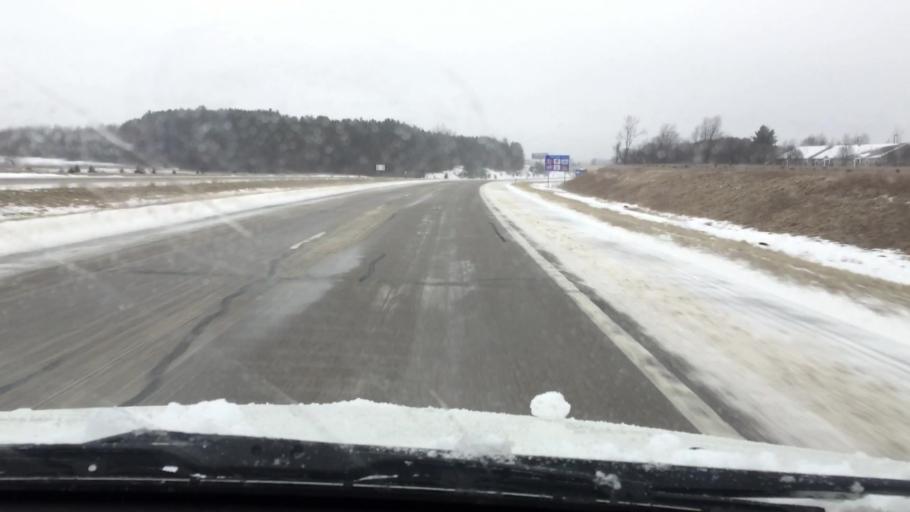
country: US
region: Michigan
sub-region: Wexford County
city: Cadillac
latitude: 44.2612
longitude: -85.3839
